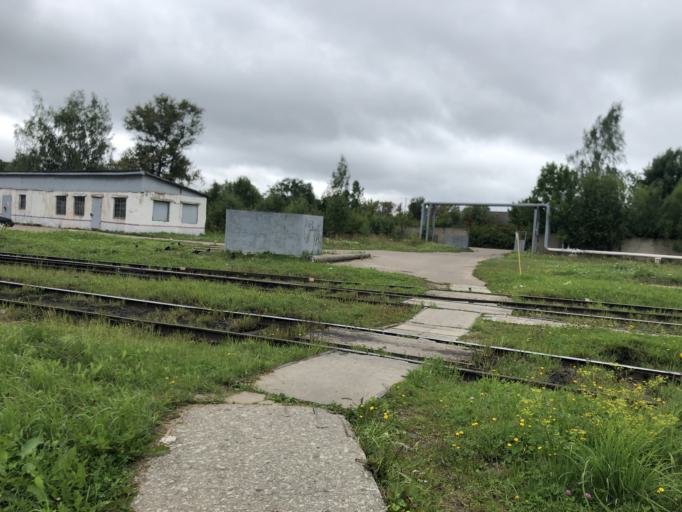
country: RU
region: Tverskaya
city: Rzhev
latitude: 56.2397
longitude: 34.3331
